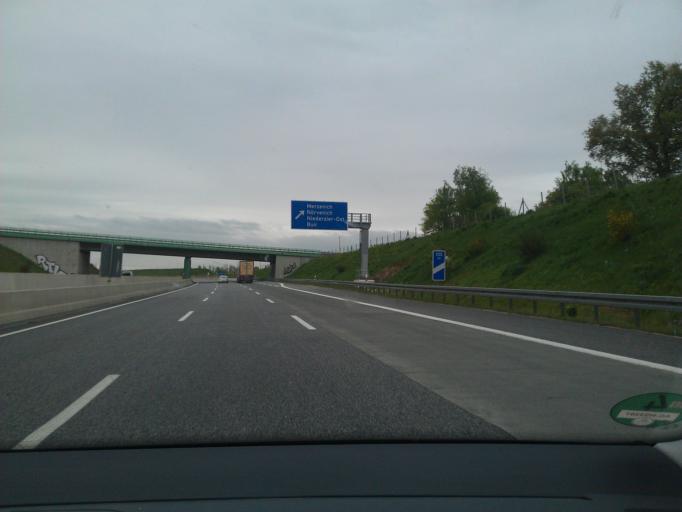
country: DE
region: North Rhine-Westphalia
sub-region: Regierungsbezirk Koln
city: Merzenich
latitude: 50.8486
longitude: 6.5133
